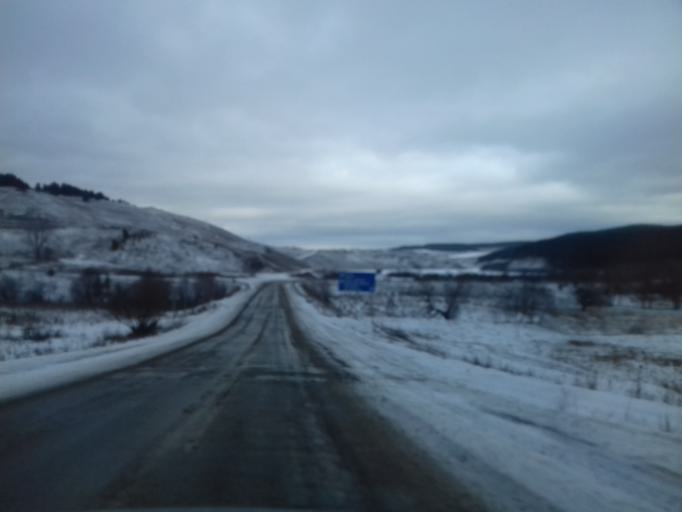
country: RU
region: Bashkortostan
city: Verkhniy Avzyan
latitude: 53.5058
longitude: 57.6821
